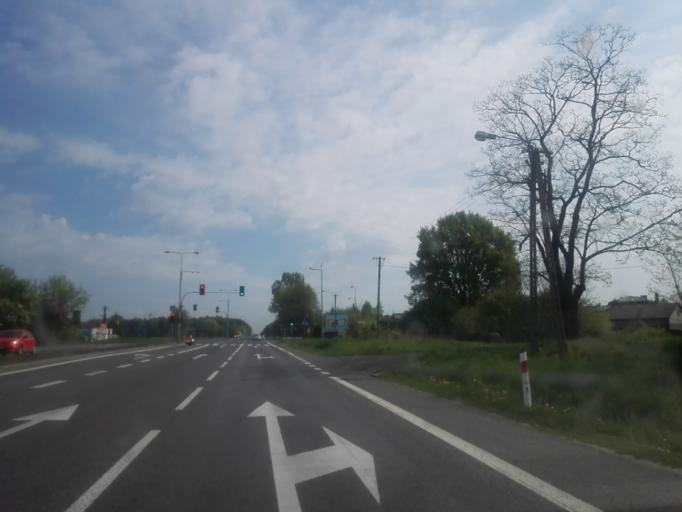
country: PL
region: Lodz Voivodeship
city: Zabia Wola
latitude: 52.0533
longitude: 20.7223
